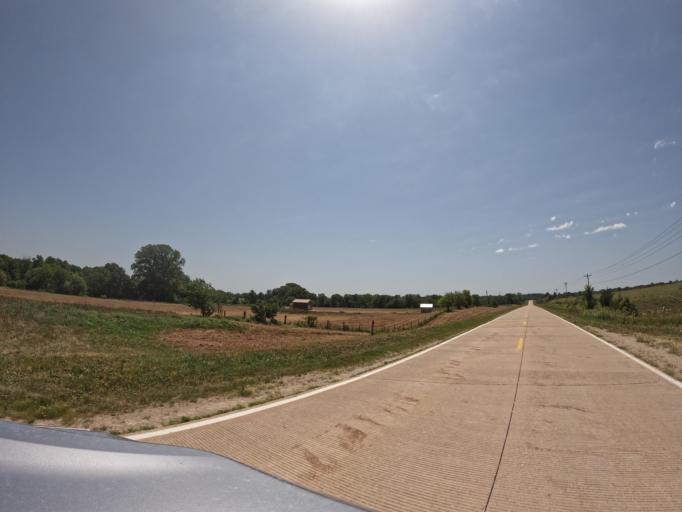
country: US
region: Iowa
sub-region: Henry County
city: Mount Pleasant
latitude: 40.9266
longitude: -91.5545
